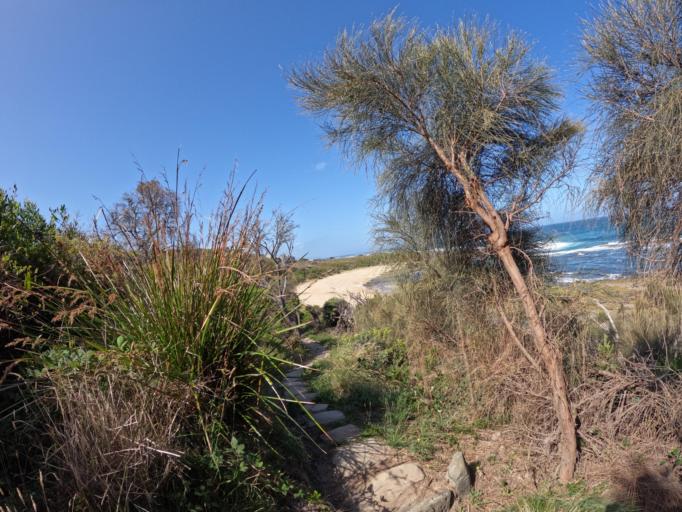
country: AU
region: Victoria
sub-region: Colac-Otway
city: Apollo Bay
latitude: -38.7891
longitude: 143.6490
